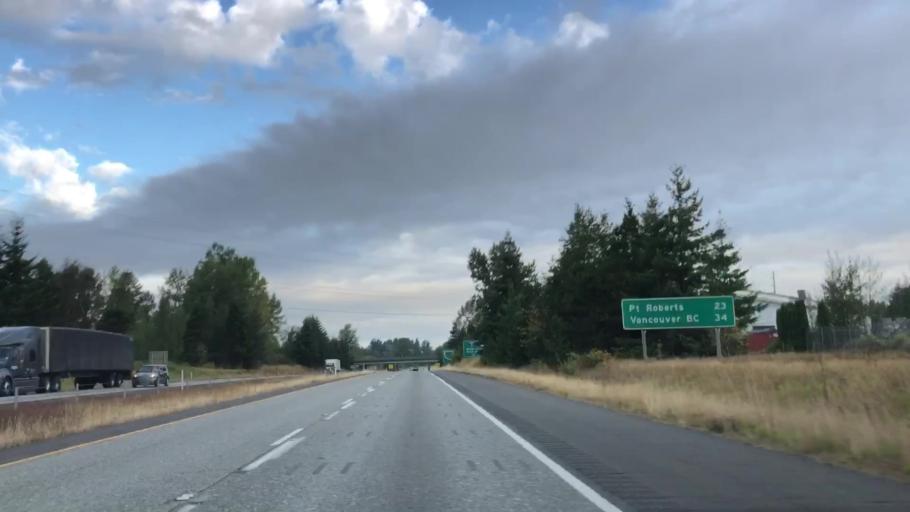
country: US
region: Washington
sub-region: Whatcom County
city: Blaine
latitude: 48.9762
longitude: -122.7246
